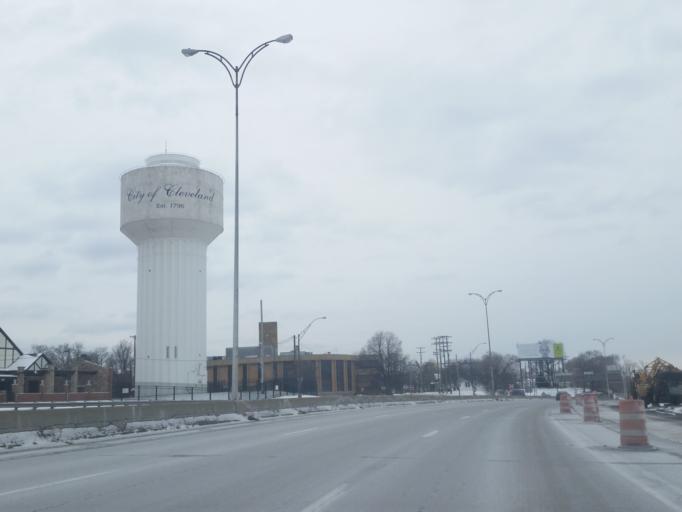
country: US
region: Ohio
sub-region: Cuyahoga County
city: Cleveland
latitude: 41.4885
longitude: -81.7163
